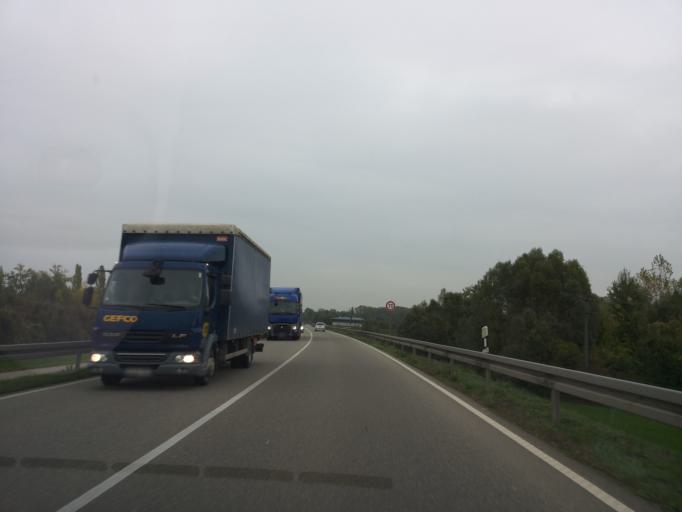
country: FR
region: Alsace
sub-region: Departement du Bas-Rhin
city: Plobsheim
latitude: 48.4939
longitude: 7.7883
